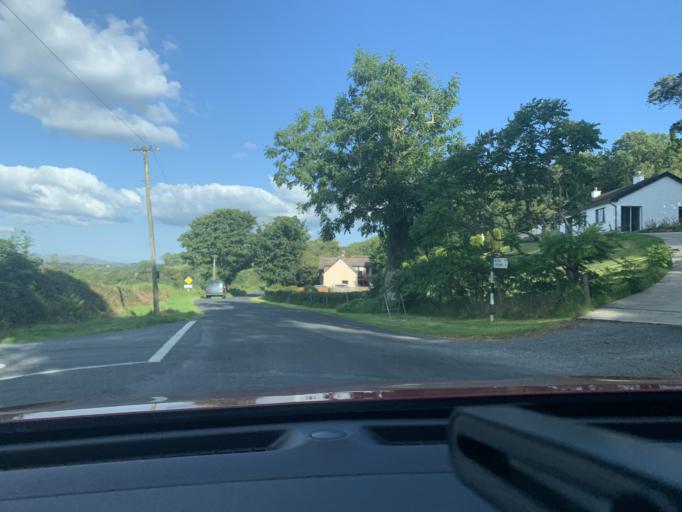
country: IE
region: Connaught
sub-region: Sligo
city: Strandhill
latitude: 54.2007
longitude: -8.5825
